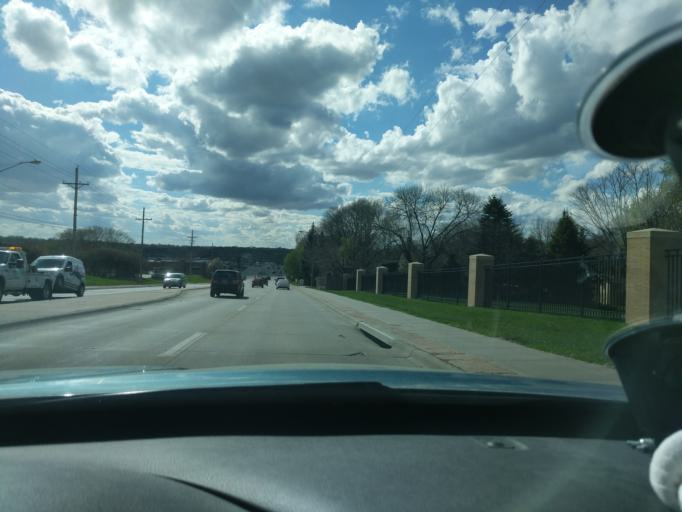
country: US
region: Nebraska
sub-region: Douglas County
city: Ralston
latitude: 41.2343
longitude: -96.0375
